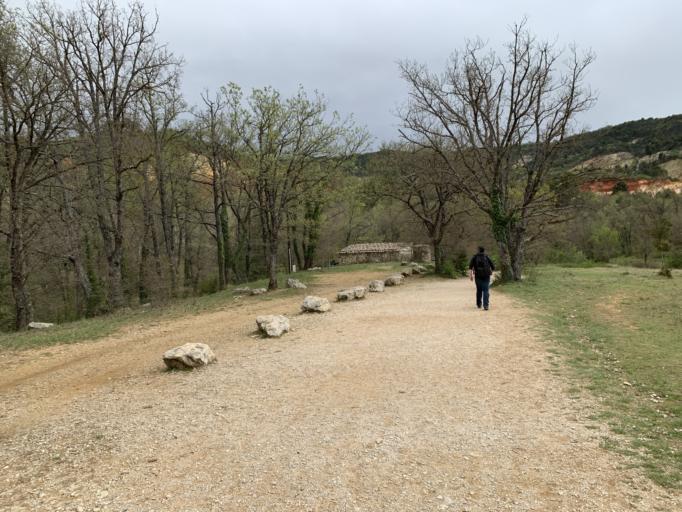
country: FR
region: Provence-Alpes-Cote d'Azur
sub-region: Departement du Vaucluse
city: Saignon
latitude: 43.9170
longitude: 5.4968
